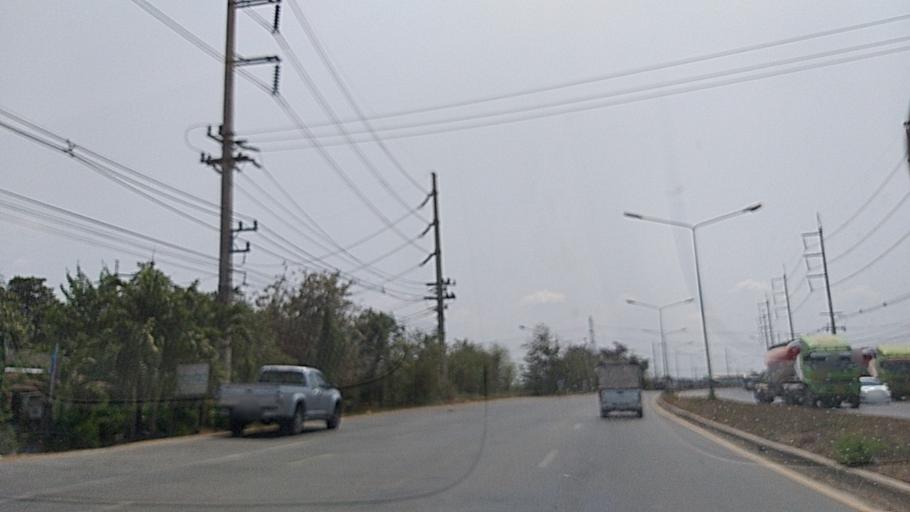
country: TH
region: Chachoengsao
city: Bang Nam Priao
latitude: 13.8321
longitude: 101.0558
